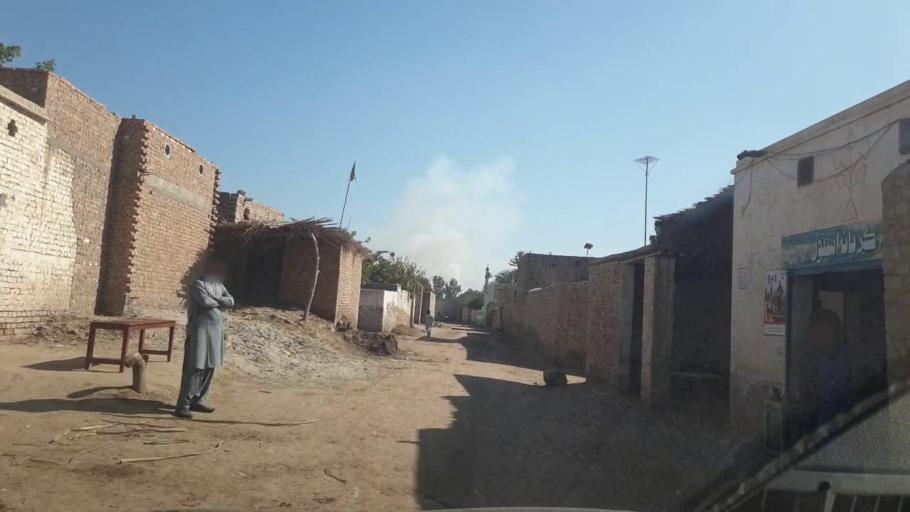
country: PK
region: Sindh
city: Mirpur Mathelo
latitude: 28.1406
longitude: 69.5317
